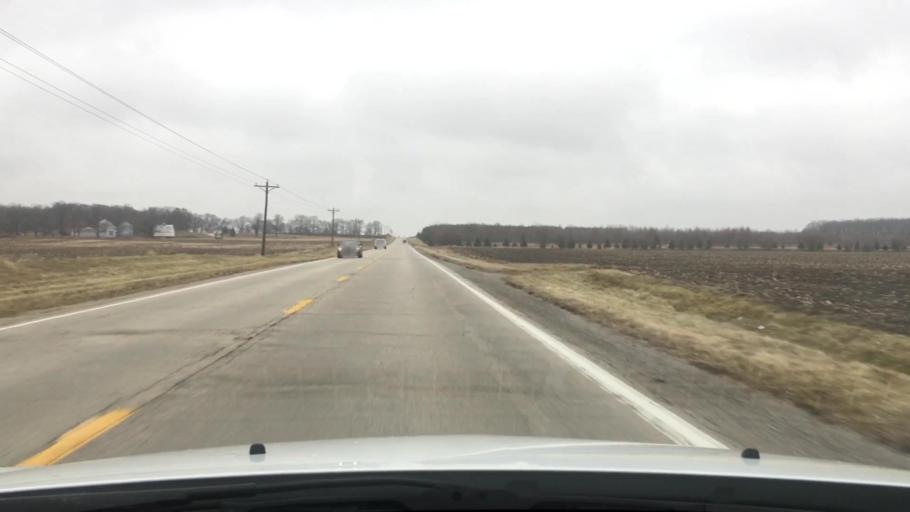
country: US
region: Illinois
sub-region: Iroquois County
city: Watseka
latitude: 40.8913
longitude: -87.6785
